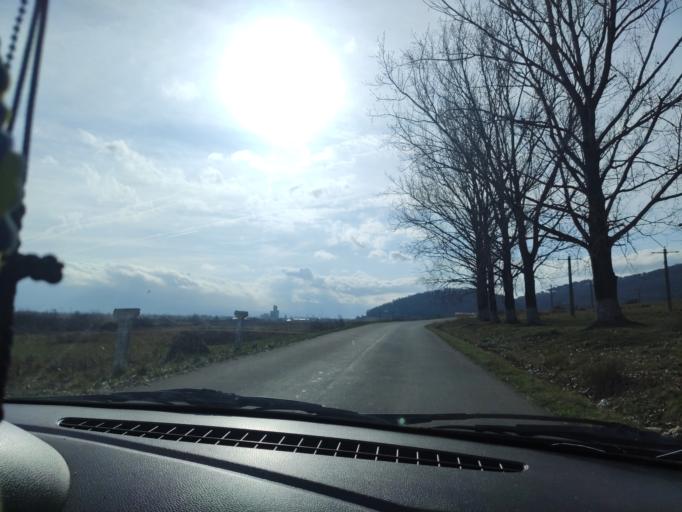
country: RO
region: Brasov
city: Codlea
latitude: 45.7283
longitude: 25.4573
